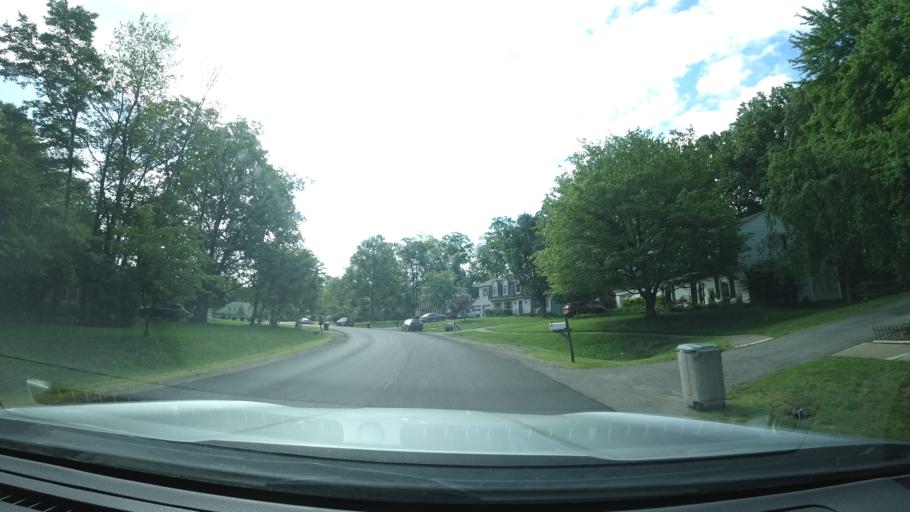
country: US
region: Virginia
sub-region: Fairfax County
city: Oak Hill
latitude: 38.9377
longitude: -77.3769
